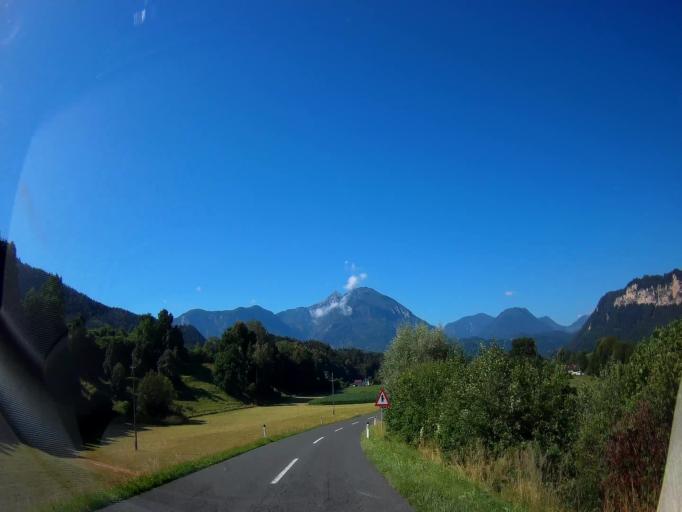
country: AT
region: Carinthia
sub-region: Politischer Bezirk Volkermarkt
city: Gallizien
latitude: 46.5924
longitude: 14.5221
